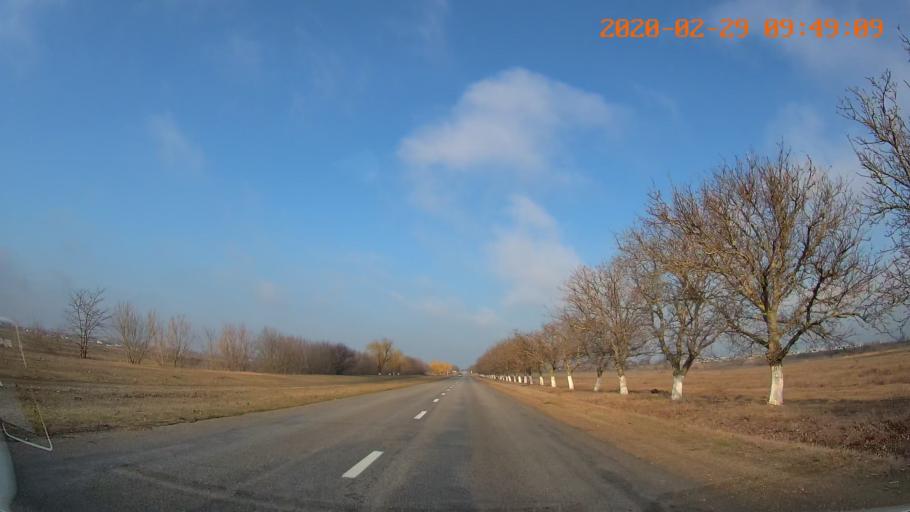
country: MD
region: Telenesti
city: Crasnoe
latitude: 46.6950
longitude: 29.7766
